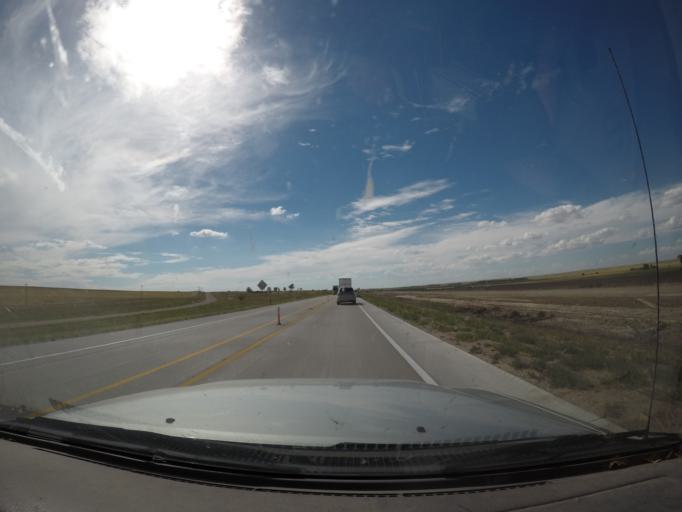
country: US
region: Nebraska
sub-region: Deuel County
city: Chappell
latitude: 41.0918
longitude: -102.5175
